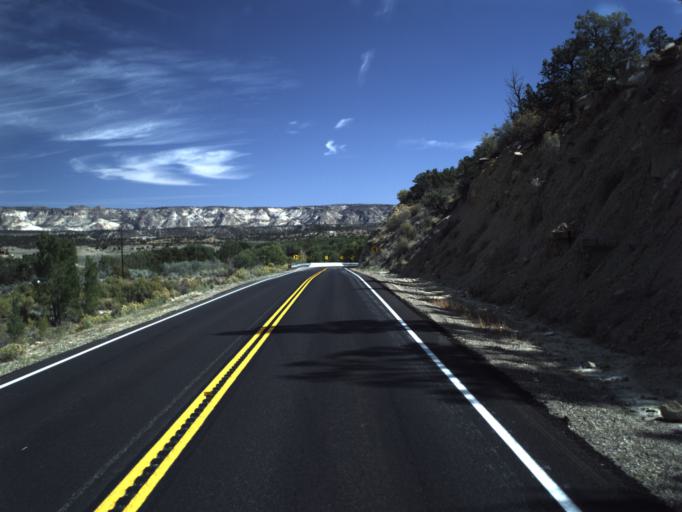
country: US
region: Utah
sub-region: Wayne County
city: Loa
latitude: 37.7639
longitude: -111.6862
